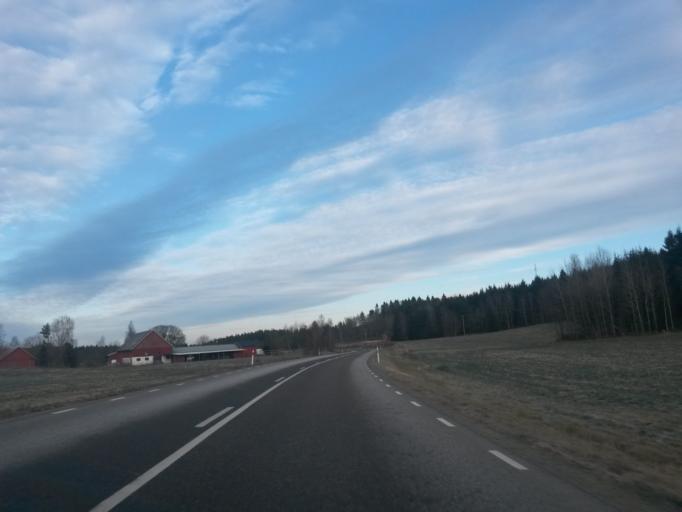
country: SE
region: Vaestra Goetaland
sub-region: Vargarda Kommun
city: Vargarda
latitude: 57.9584
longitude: 12.8123
